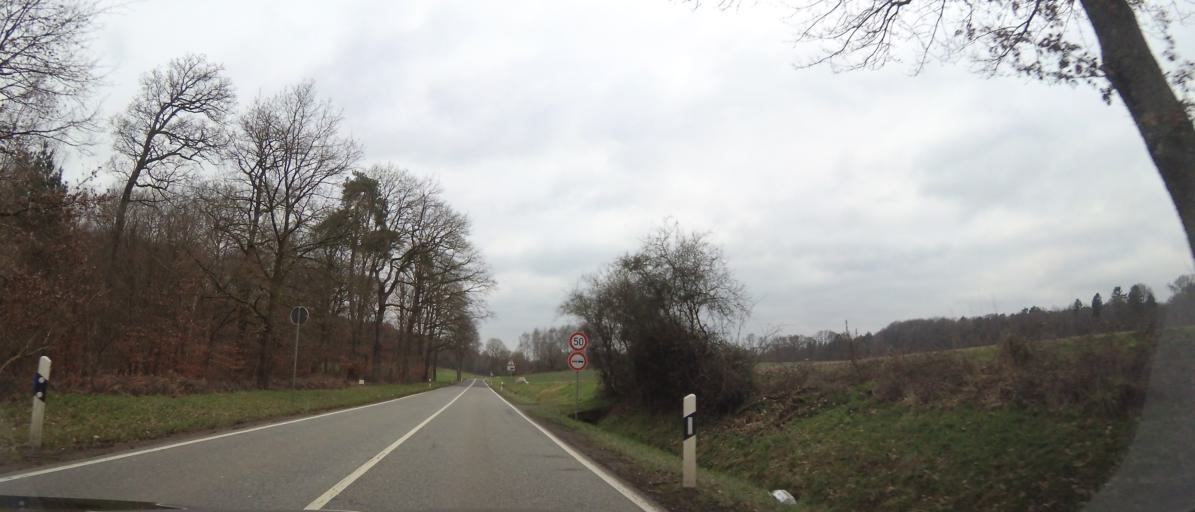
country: DE
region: Saarland
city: Puttlingen
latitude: 49.3173
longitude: 6.8665
